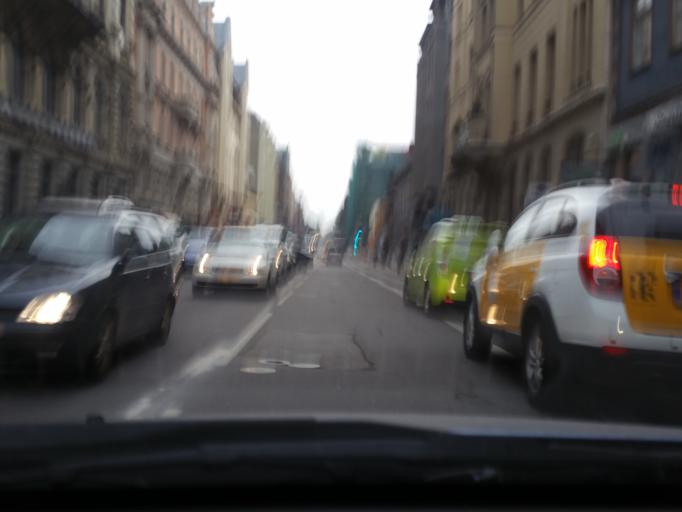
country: LV
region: Riga
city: Riga
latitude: 56.9547
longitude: 24.1244
